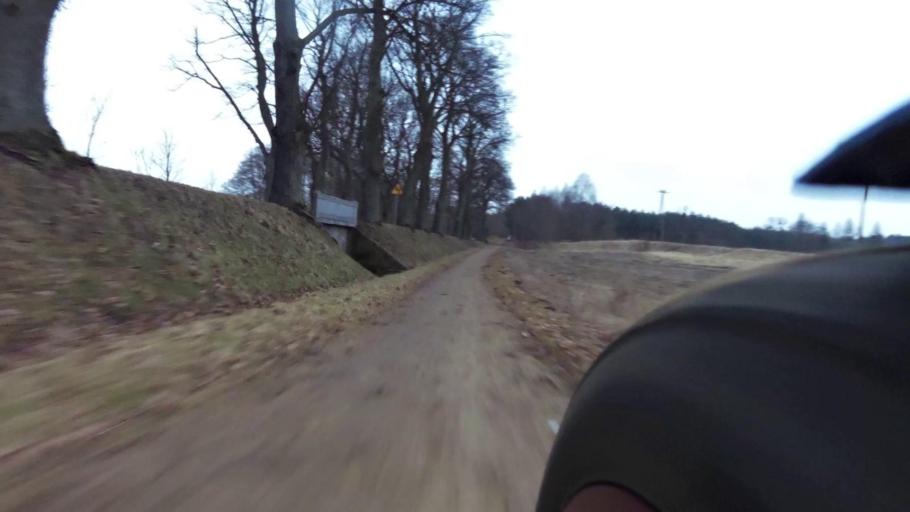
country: PL
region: West Pomeranian Voivodeship
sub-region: Powiat walecki
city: Walcz
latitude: 53.2434
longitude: 16.3748
